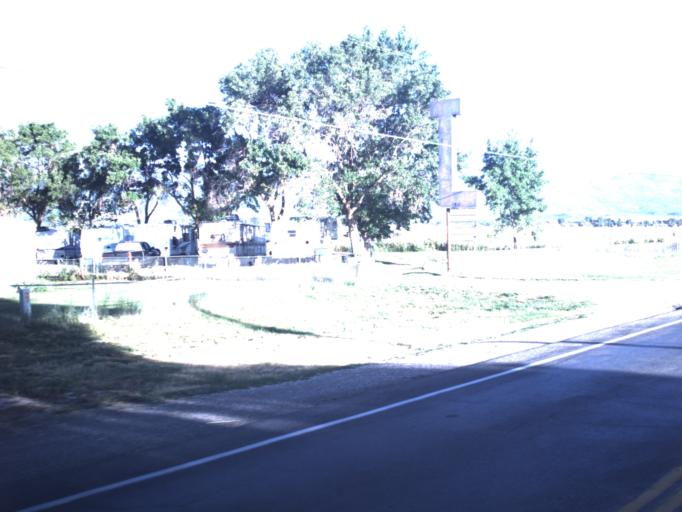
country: US
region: Utah
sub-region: Sanpete County
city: Mount Pleasant
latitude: 39.5650
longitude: -111.4555
